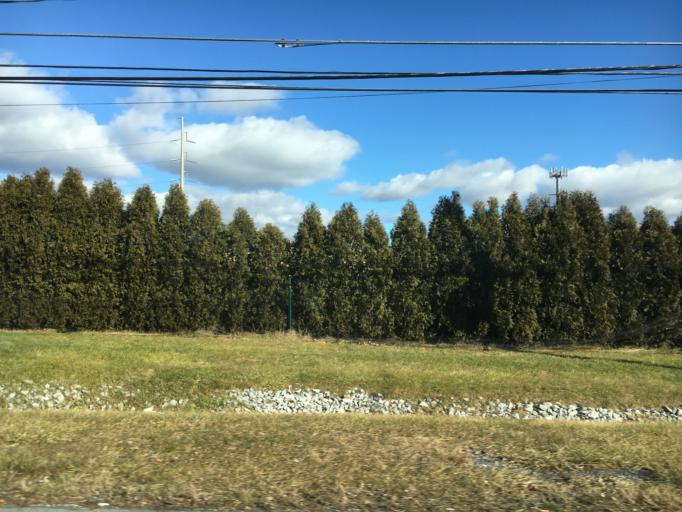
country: US
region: Pennsylvania
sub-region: Lehigh County
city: Stiles
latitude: 40.6390
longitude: -75.5108
